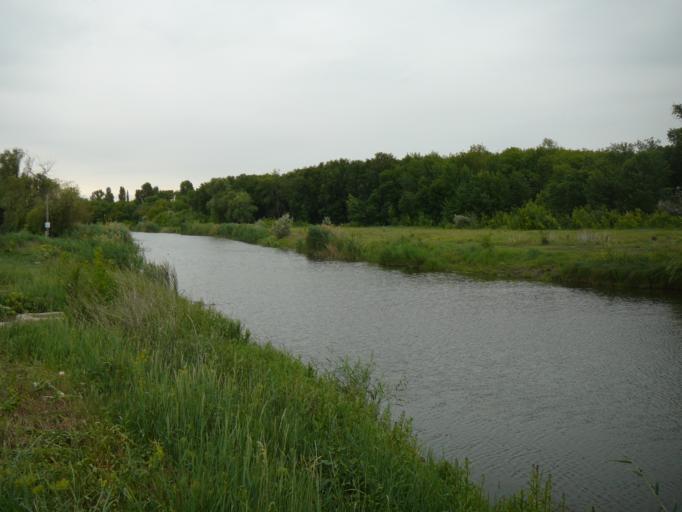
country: RU
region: Saratov
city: Engel's
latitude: 51.4737
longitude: 46.0948
